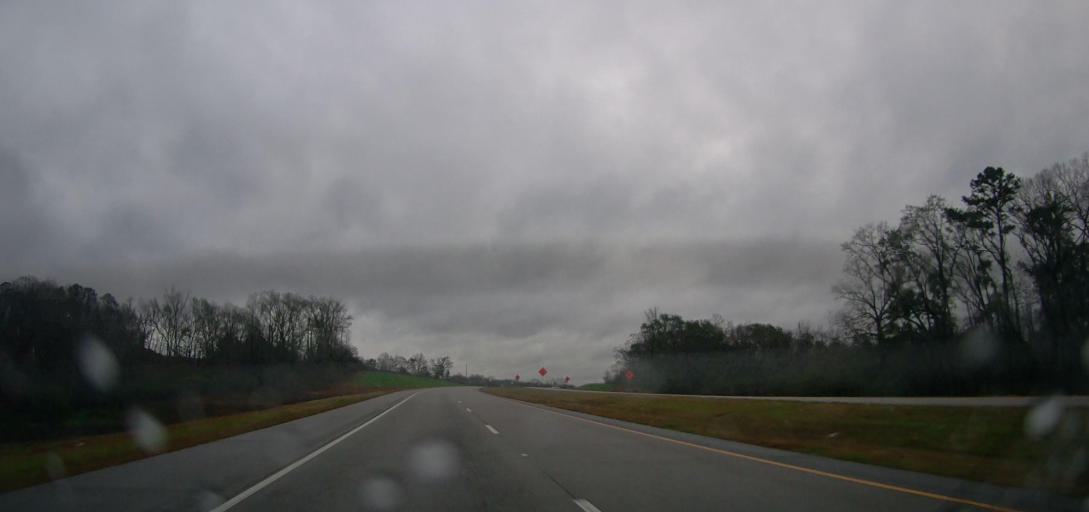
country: US
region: Alabama
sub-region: Bibb County
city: Centreville
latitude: 32.9398
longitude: -87.0701
